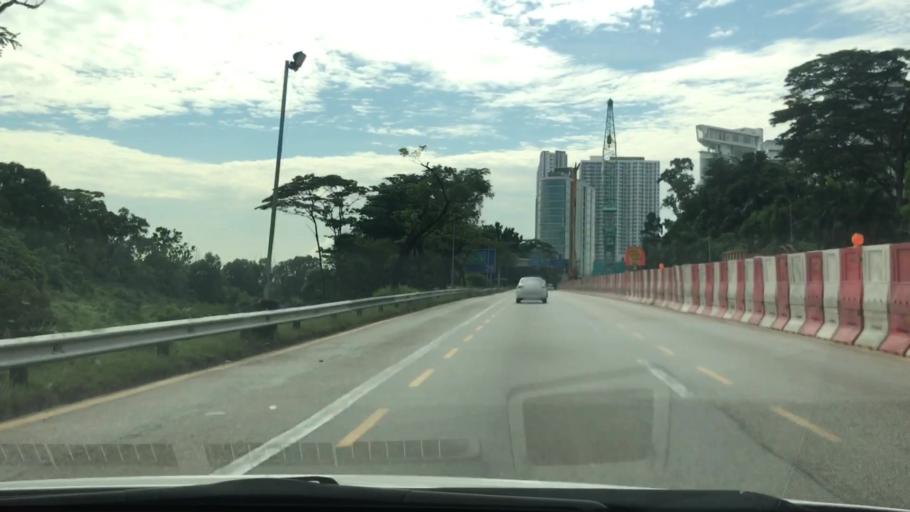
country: MY
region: Kuala Lumpur
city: Kuala Lumpur
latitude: 3.1104
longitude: 101.6896
